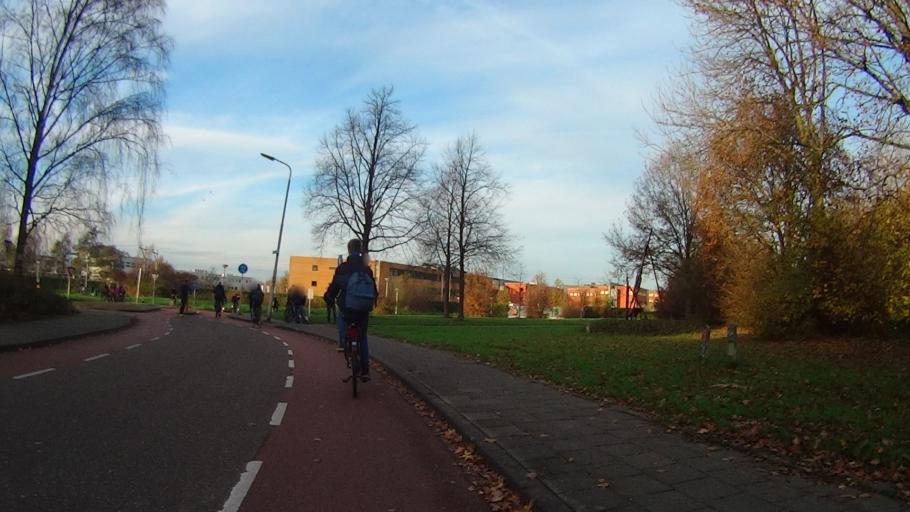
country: NL
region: Utrecht
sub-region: Gemeente Amersfoort
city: Randenbroek
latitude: 52.1712
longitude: 5.4041
